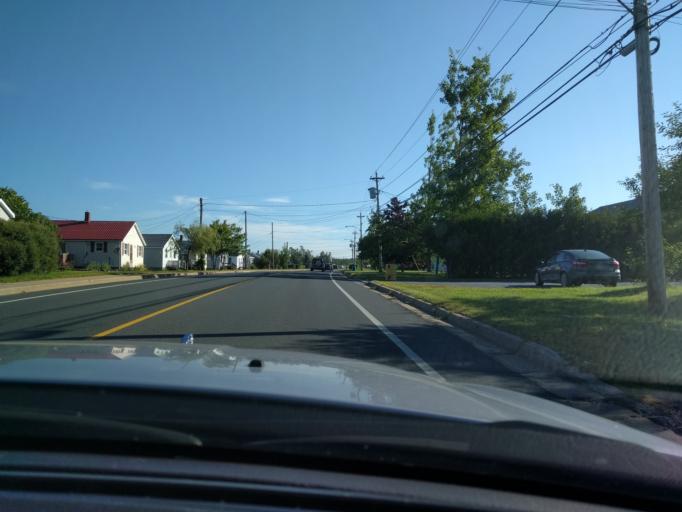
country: US
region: Maine
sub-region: Washington County
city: Eastport
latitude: 45.0636
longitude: -66.7802
